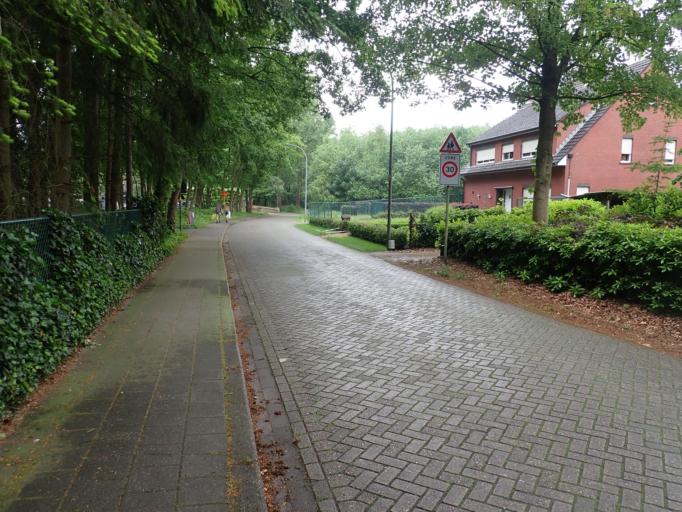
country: BE
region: Flanders
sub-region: Provincie Antwerpen
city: Oud-Turnhout
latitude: 51.3134
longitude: 5.0035
